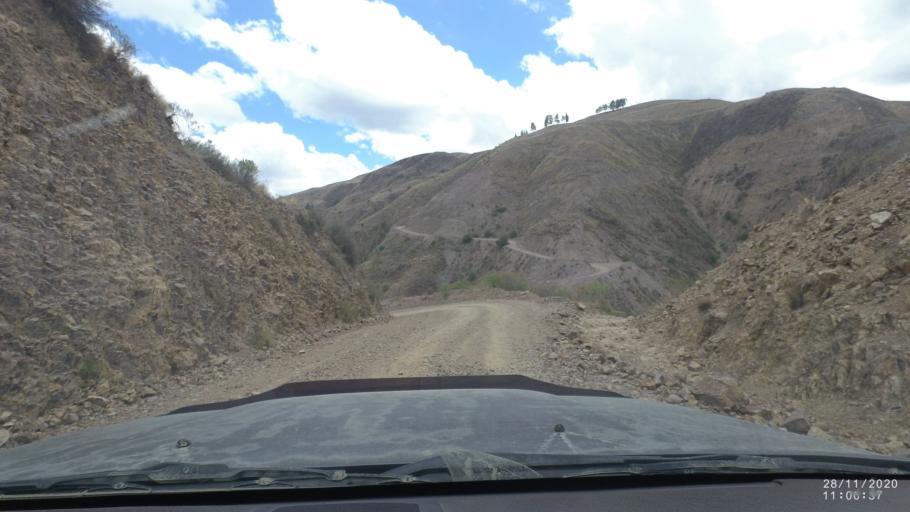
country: BO
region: Cochabamba
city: Capinota
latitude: -17.7680
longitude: -66.1061
